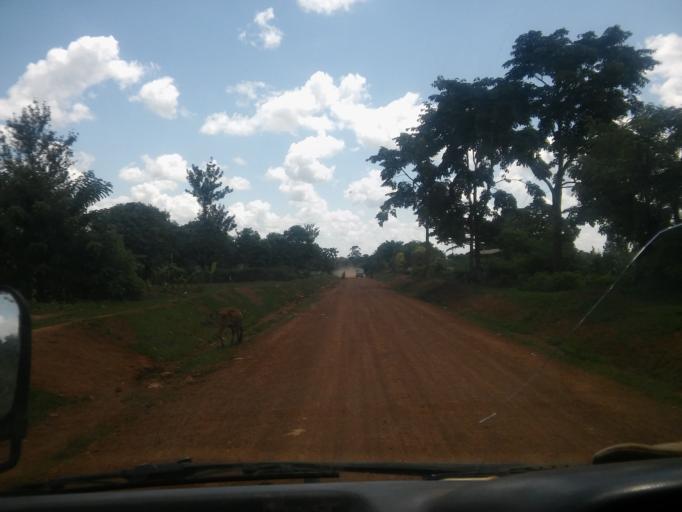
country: UG
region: Eastern Region
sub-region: Budaka District
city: Budaka
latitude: 1.1092
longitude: 33.9670
